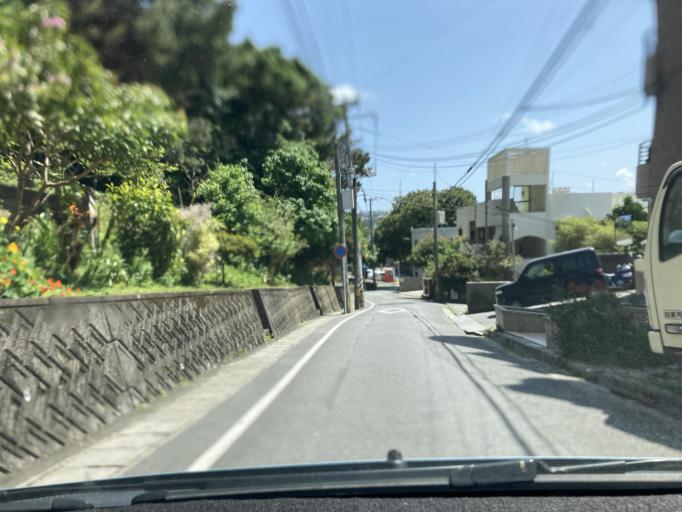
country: JP
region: Okinawa
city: Naha-shi
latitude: 26.2003
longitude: 127.6885
